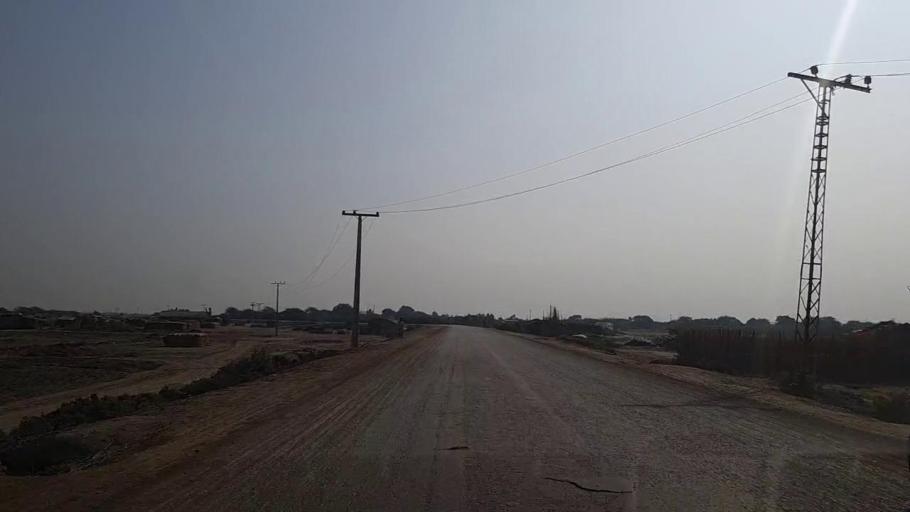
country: PK
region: Sindh
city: Keti Bandar
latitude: 24.2339
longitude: 67.6081
